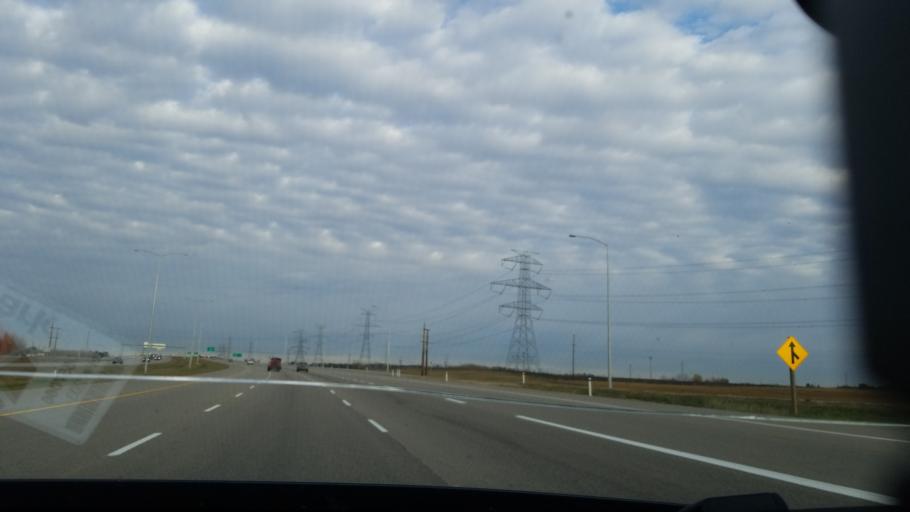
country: CA
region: Alberta
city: Sherwood Park
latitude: 53.6185
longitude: -113.3603
